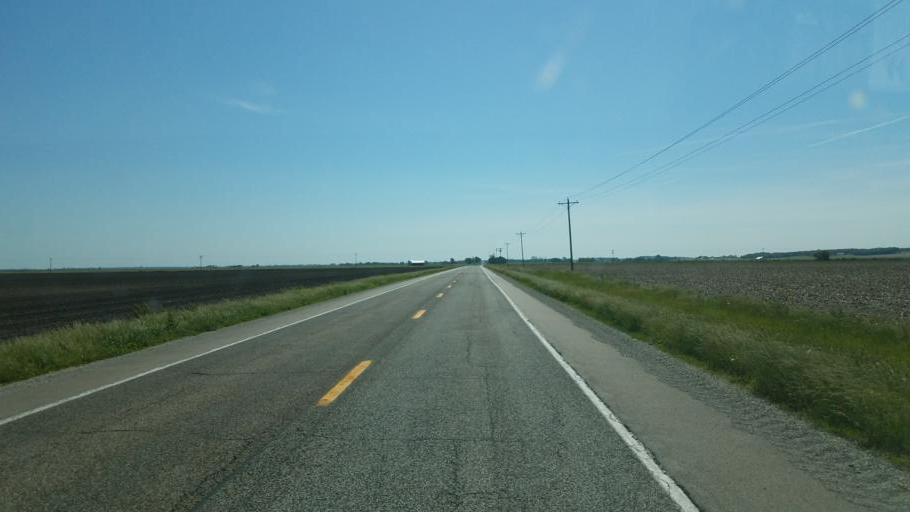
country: US
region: Illinois
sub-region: Mason County
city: Mason City
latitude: 40.3046
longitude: -89.7194
